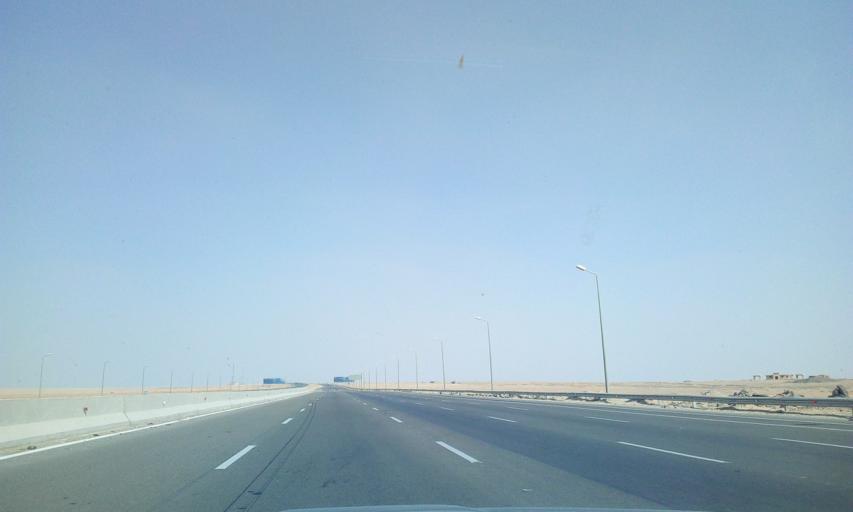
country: EG
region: Muhafazat al Qahirah
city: Halwan
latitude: 29.9022
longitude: 31.7721
